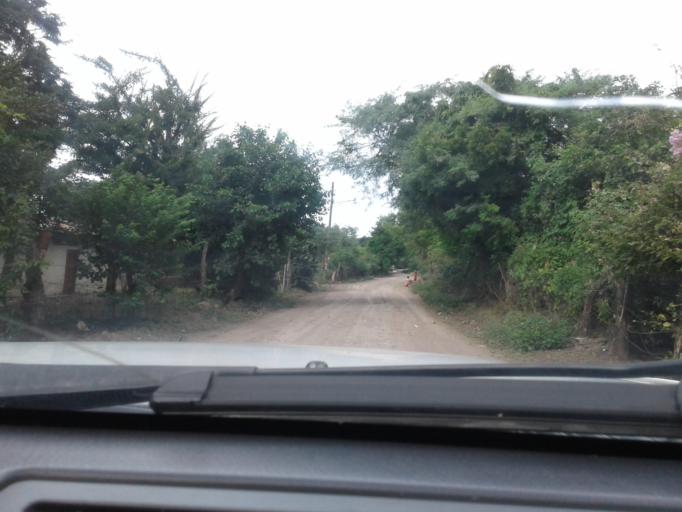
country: NI
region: Matagalpa
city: Ciudad Dario
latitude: 12.8462
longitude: -86.1206
